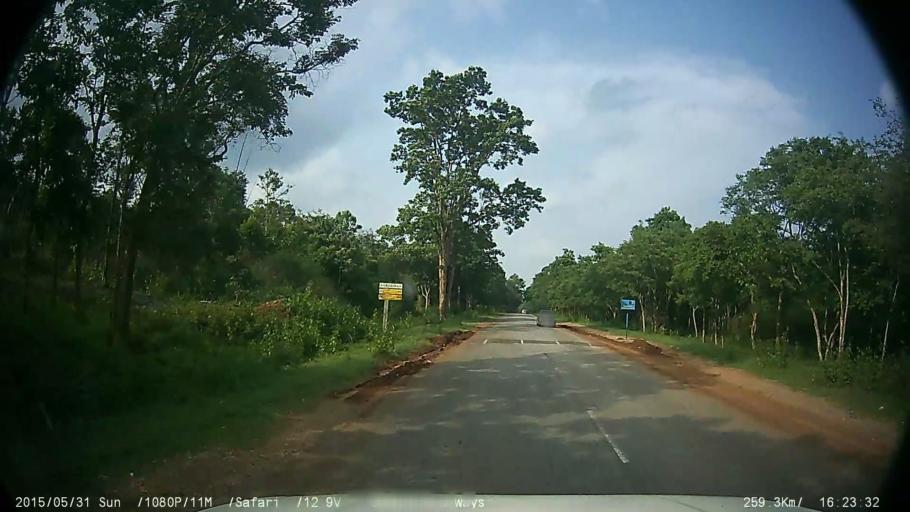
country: IN
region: Karnataka
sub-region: Chamrajnagar
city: Gundlupet
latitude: 11.7591
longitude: 76.5176
